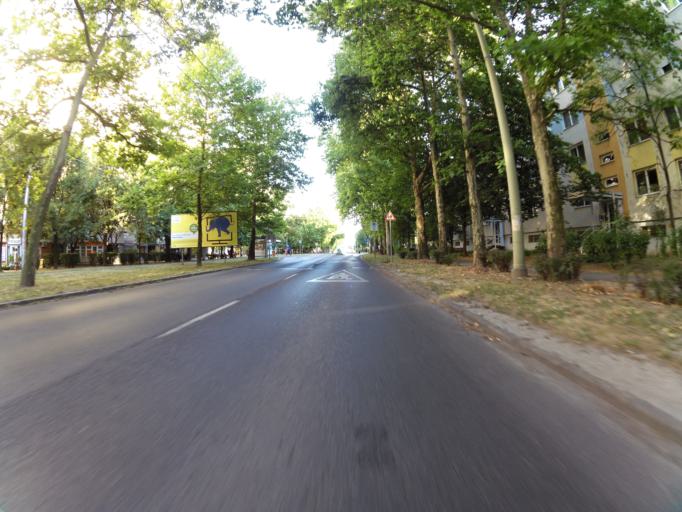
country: HU
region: Csongrad
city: Szeged
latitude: 46.2646
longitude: 20.1688
